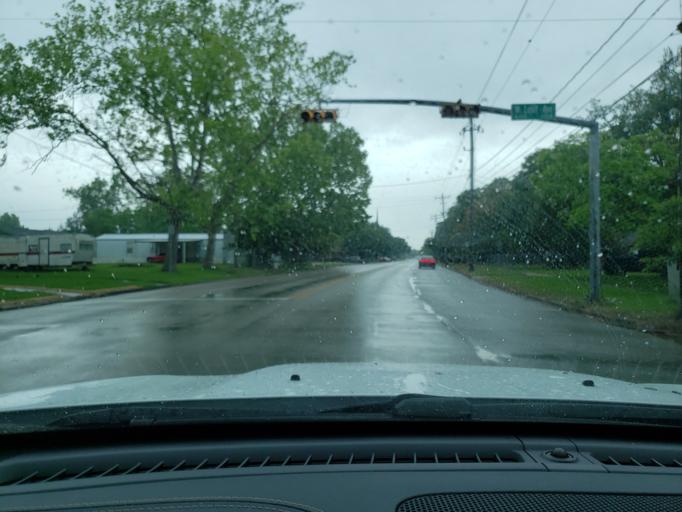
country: US
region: Texas
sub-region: Harris County
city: Baytown
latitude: 29.7384
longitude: -94.9707
